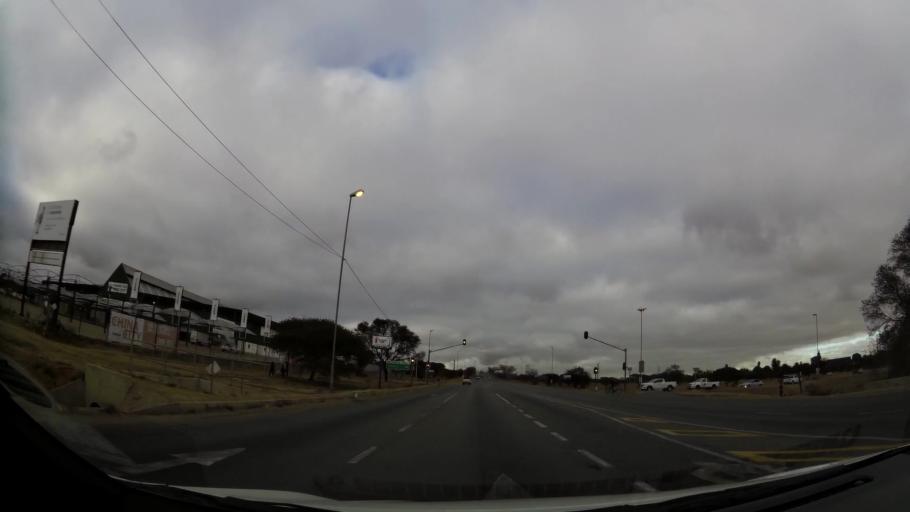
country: ZA
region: Limpopo
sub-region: Capricorn District Municipality
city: Polokwane
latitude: -23.8752
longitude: 29.4627
